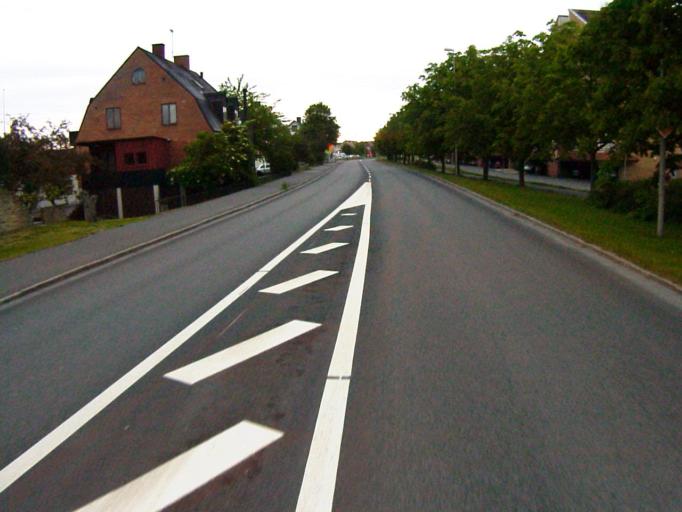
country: SE
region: Skane
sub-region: Kristianstads Kommun
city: Kristianstad
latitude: 56.0207
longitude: 14.1392
